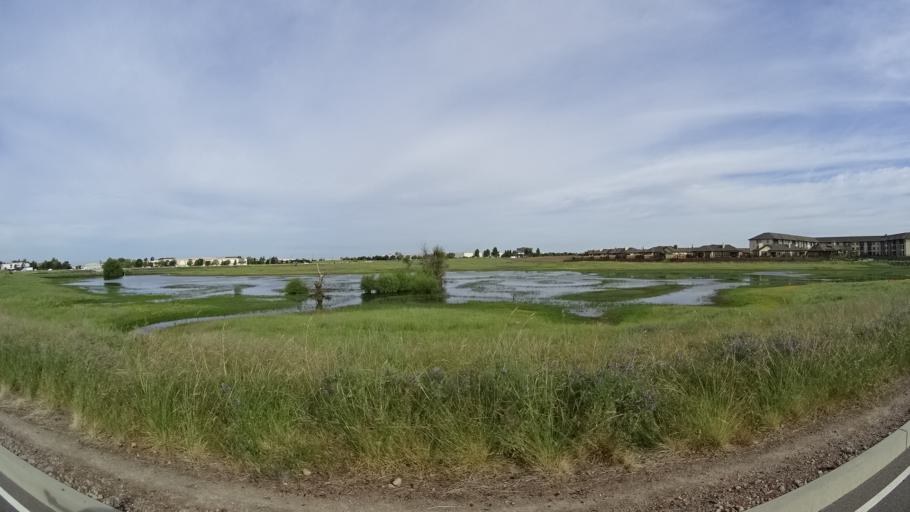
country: US
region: California
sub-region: Placer County
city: Rocklin
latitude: 38.8220
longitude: -121.2950
